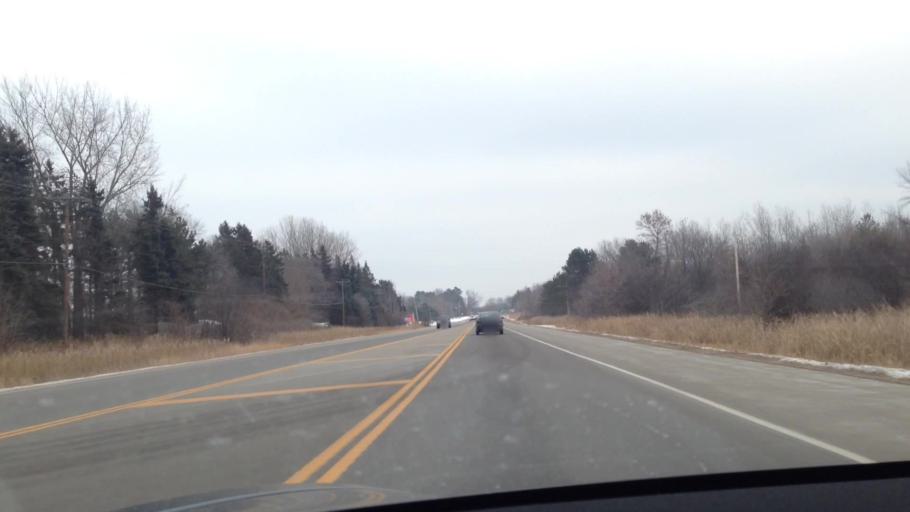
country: US
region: Minnesota
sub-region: Washington County
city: Forest Lake
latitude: 45.2609
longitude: -92.9670
